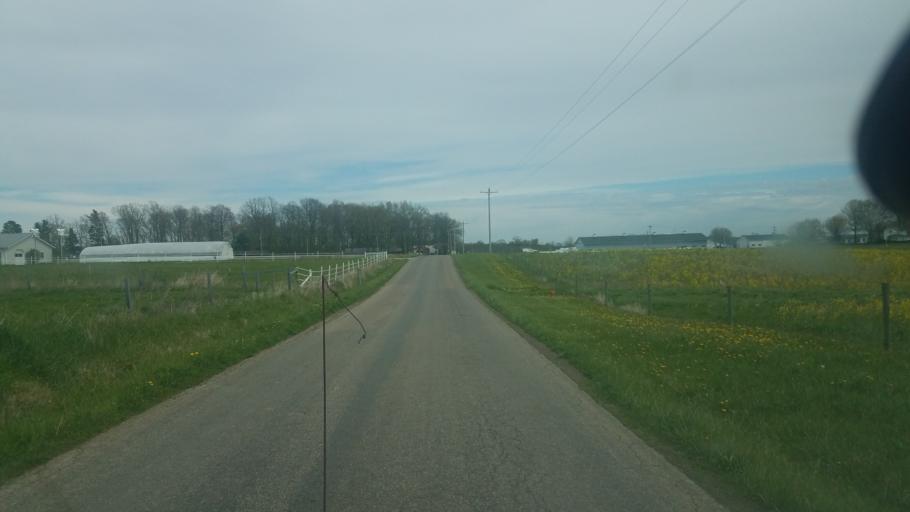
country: US
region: Ohio
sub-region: Wayne County
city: Apple Creek
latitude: 40.7334
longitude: -81.9002
